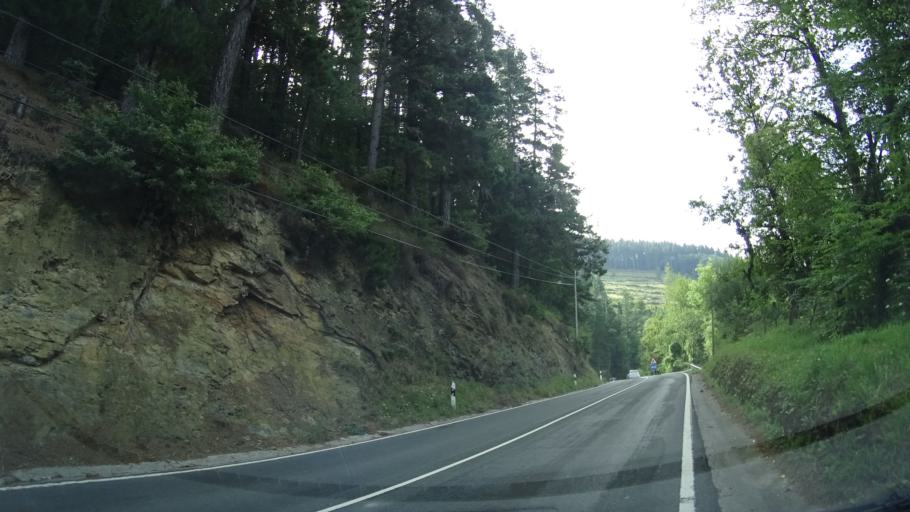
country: ES
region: Basque Country
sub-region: Bizkaia
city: Manaria
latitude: 43.1213
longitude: -2.6510
